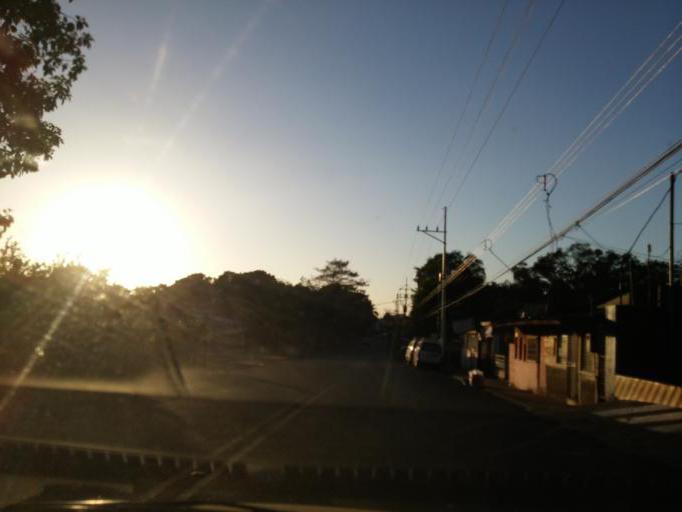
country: CR
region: Alajuela
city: Orotina
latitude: 9.9136
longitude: -84.5256
